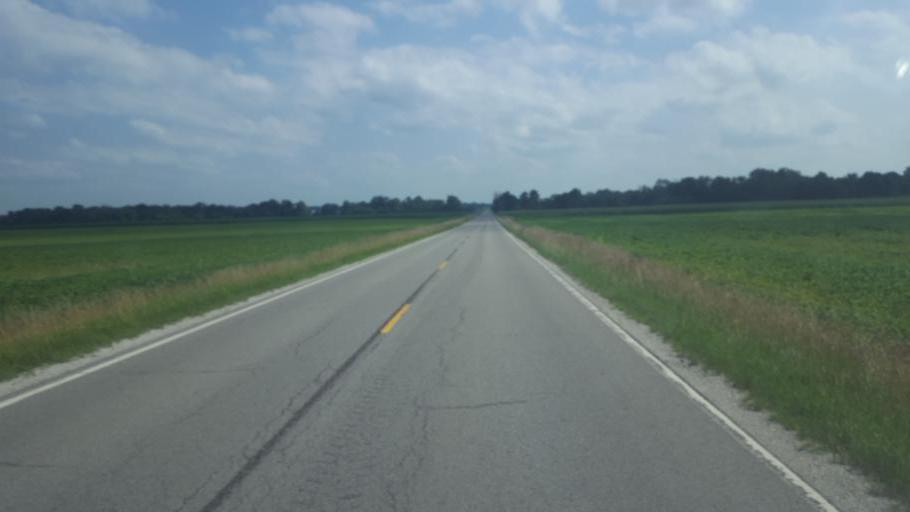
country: US
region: Ohio
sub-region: Huron County
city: Plymouth
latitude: 40.9405
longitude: -82.7720
